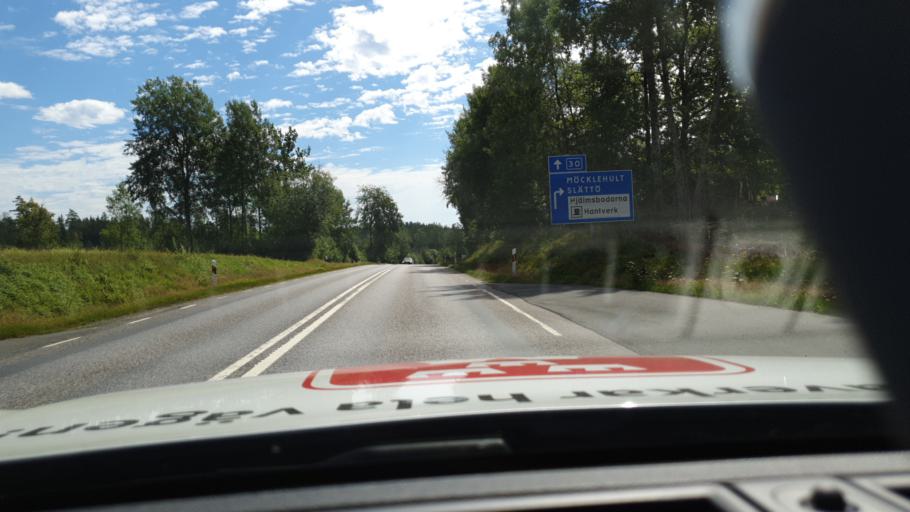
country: SE
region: Kronoberg
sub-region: Vaxjo Kommun
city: Lammhult
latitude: 57.1975
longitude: 14.5281
